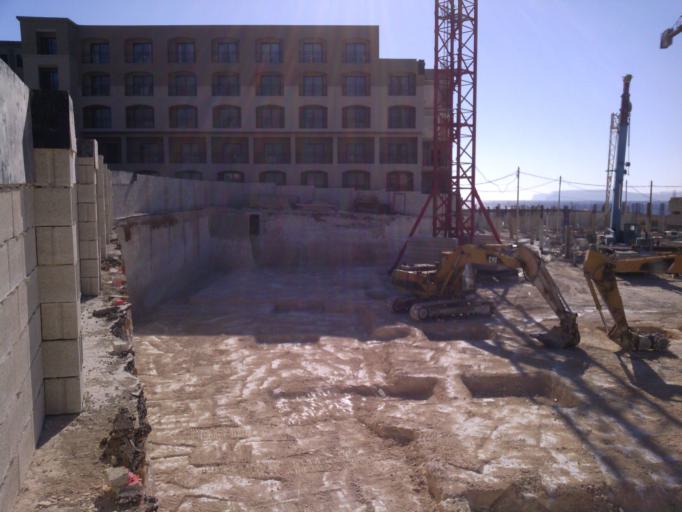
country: MT
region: Il-Mellieha
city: Mellieha
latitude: 35.9872
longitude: 14.3486
